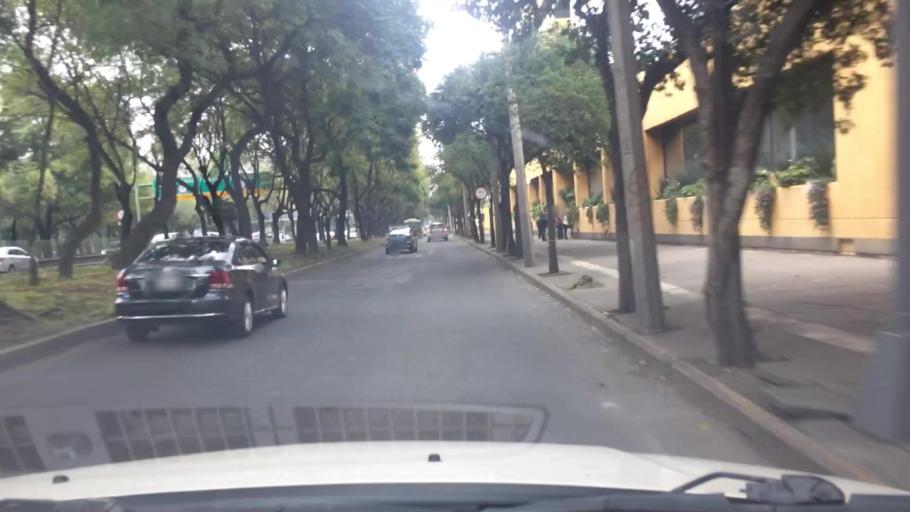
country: MX
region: Mexico City
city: Tlalpan
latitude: 19.2824
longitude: -99.1342
